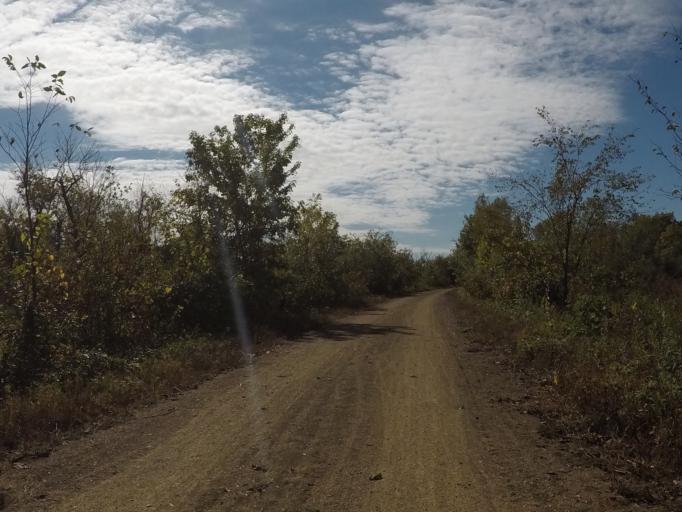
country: US
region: Wisconsin
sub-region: Richland County
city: Richland Center
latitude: 43.2620
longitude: -90.3019
